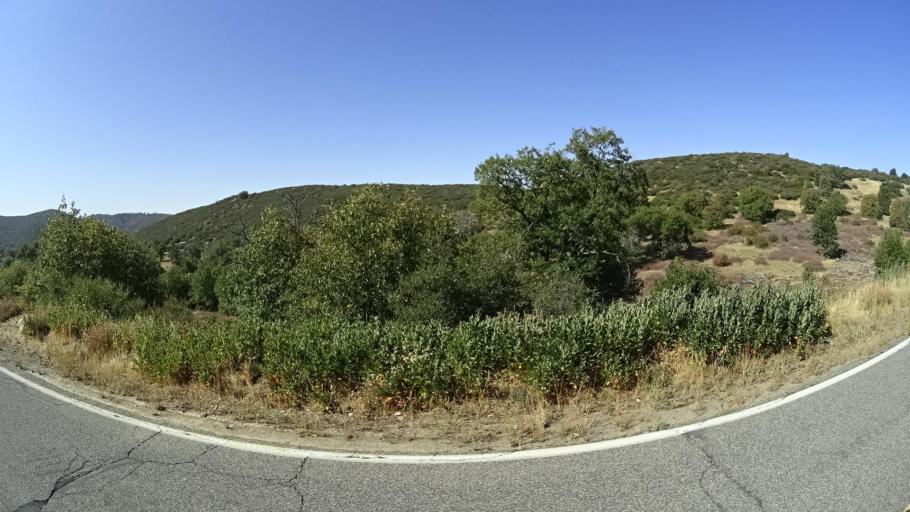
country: US
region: California
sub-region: San Diego County
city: Pine Valley
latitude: 32.9418
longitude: -116.4906
